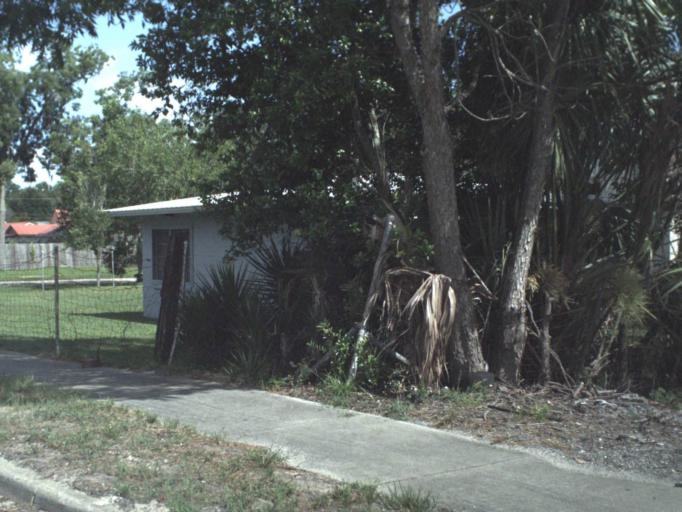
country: US
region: Florida
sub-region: Bradford County
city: Starke
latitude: 29.9430
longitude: -82.1087
